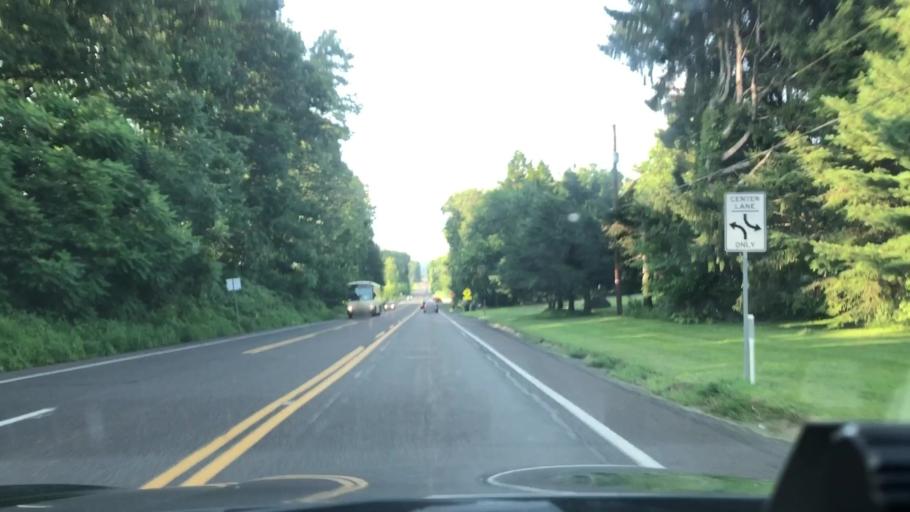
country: US
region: Pennsylvania
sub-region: Lehigh County
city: Coopersburg
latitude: 40.5465
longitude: -75.3951
